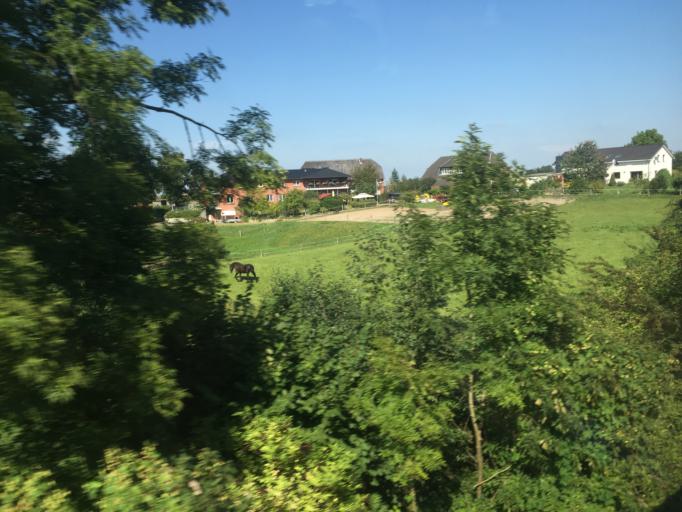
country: DE
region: Schleswig-Holstein
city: Rumpel
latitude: 53.7740
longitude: 10.3483
